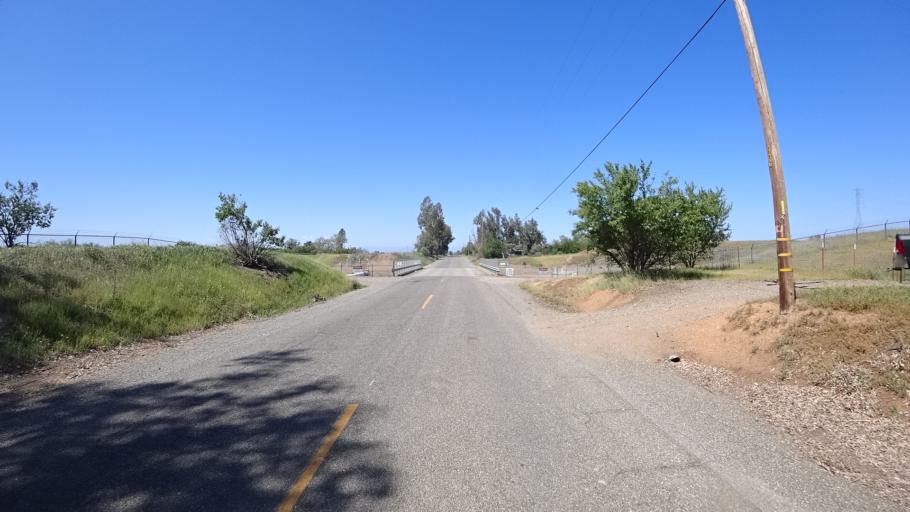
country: US
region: California
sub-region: Glenn County
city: Orland
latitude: 39.7869
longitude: -122.1549
